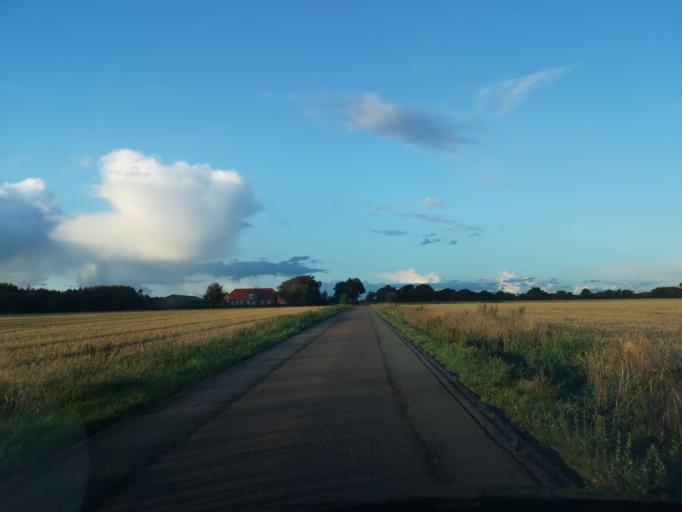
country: DK
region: Central Jutland
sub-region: Ringkobing-Skjern Kommune
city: Videbaek
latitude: 56.0267
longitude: 8.5630
